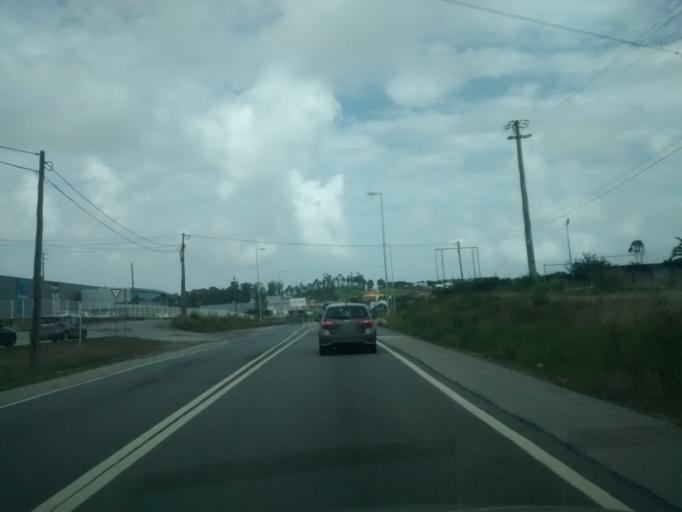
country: PT
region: Aveiro
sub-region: Oliveira do Bairro
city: Oia
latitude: 40.5678
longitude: -8.5669
